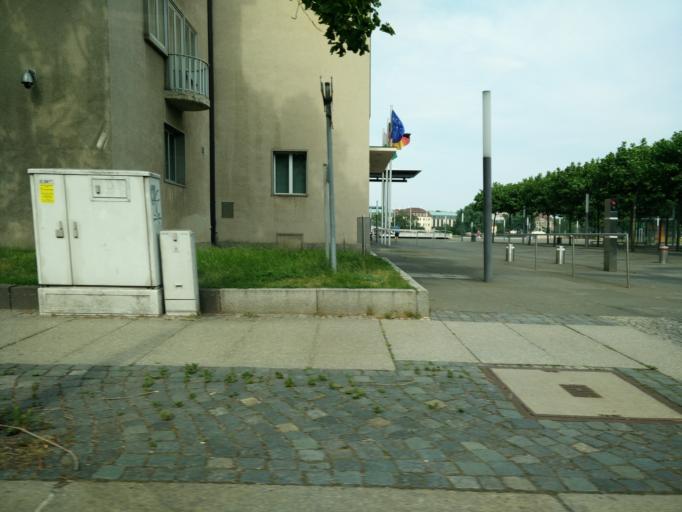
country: DE
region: Saxony
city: Dresden
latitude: 51.0561
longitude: 13.7328
